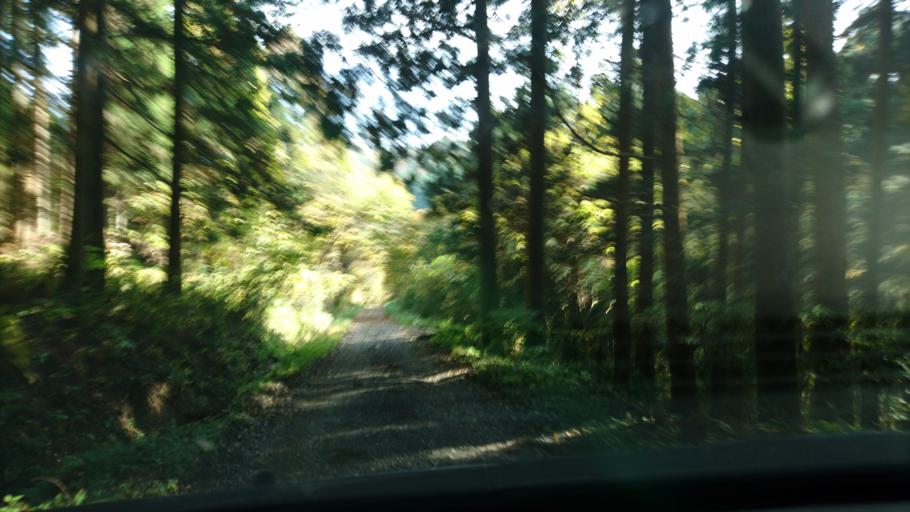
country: JP
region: Iwate
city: Ichinoseki
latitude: 38.9831
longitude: 141.1752
